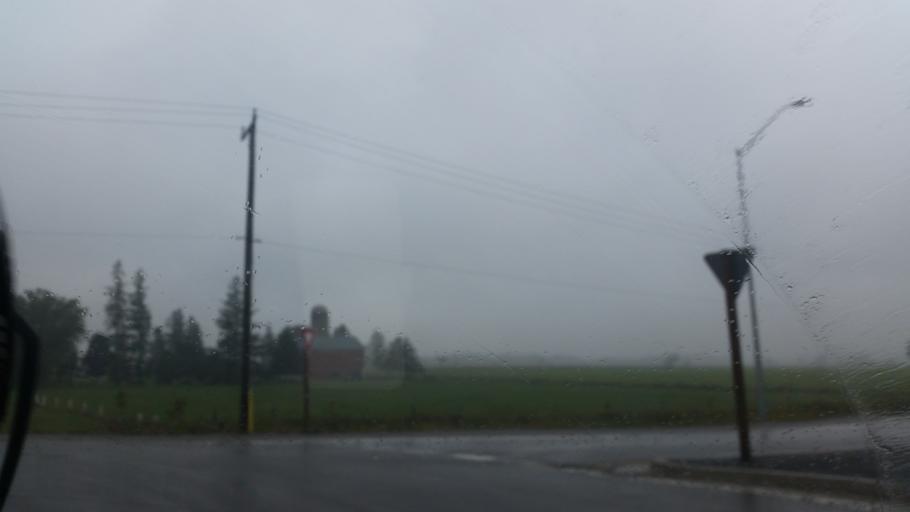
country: CA
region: Ontario
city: Stratford
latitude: 43.3088
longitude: -81.0358
